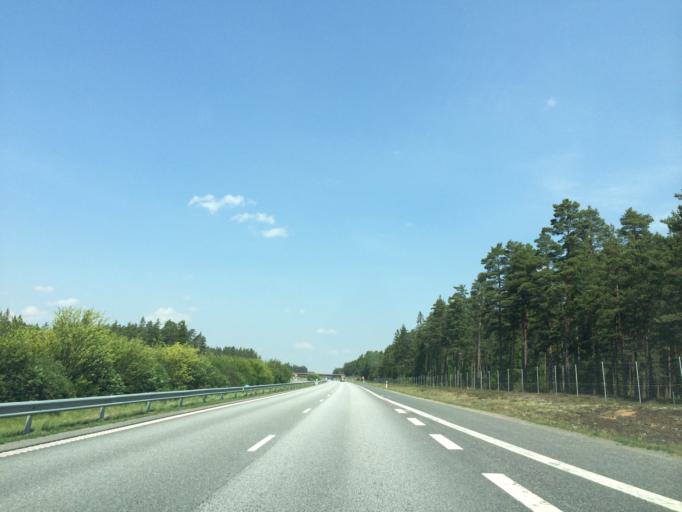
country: SE
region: Joenkoeping
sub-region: Varnamo Kommun
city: Varnamo
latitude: 57.2586
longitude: 14.0833
